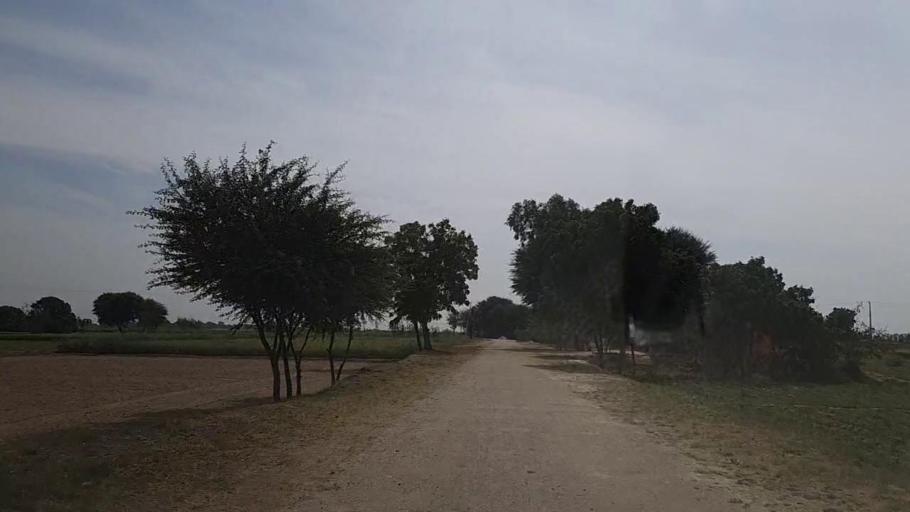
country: PK
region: Sindh
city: Kunri
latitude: 25.2110
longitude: 69.4930
